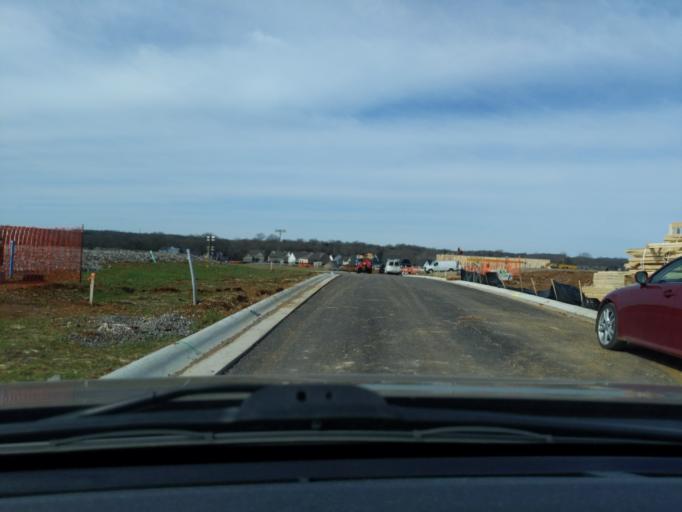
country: US
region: Tennessee
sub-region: Wilson County
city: Mount Juliet
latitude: 36.2083
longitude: -86.4882
